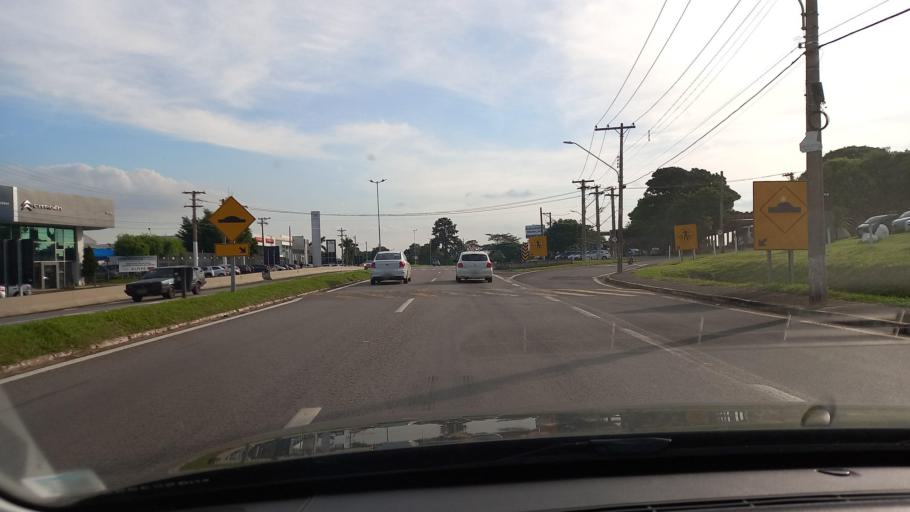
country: BR
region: Sao Paulo
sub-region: Mogi-Mirim
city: Mogi Mirim
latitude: -22.4477
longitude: -46.9793
